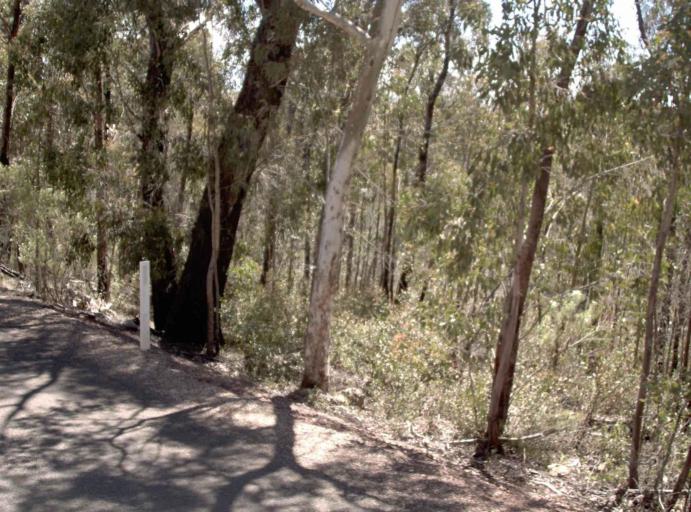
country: AU
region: New South Wales
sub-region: Snowy River
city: Jindabyne
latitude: -37.1088
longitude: 148.2515
